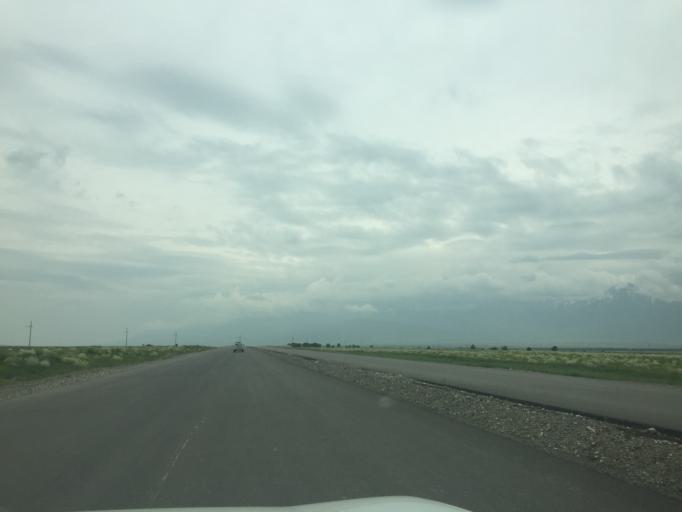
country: KZ
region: Ongtustik Qazaqstan
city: Turar Ryskulov
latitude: 42.5101
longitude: 70.3948
